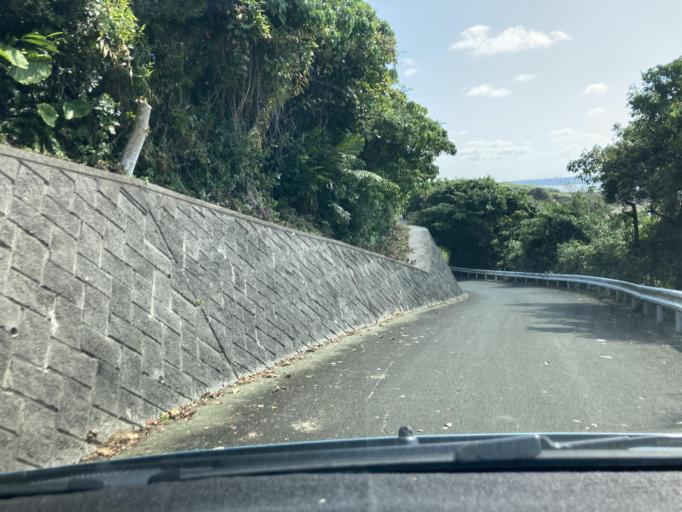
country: JP
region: Okinawa
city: Itoman
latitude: 26.1202
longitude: 127.7494
